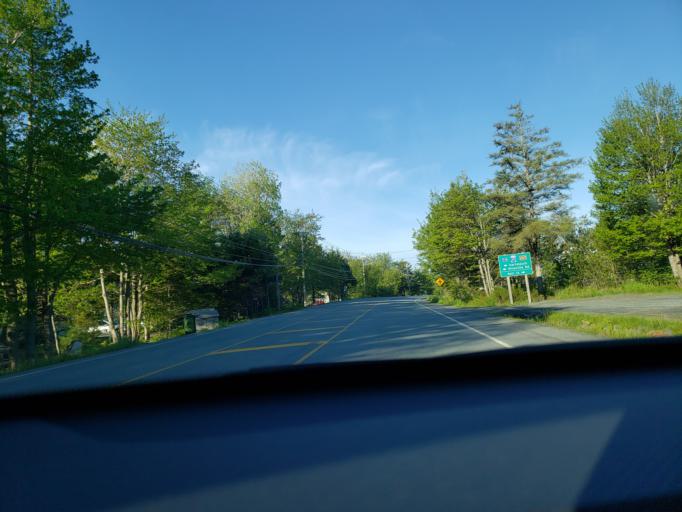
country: CA
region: Nova Scotia
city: Cole Harbour
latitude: 44.7232
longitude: -63.3977
